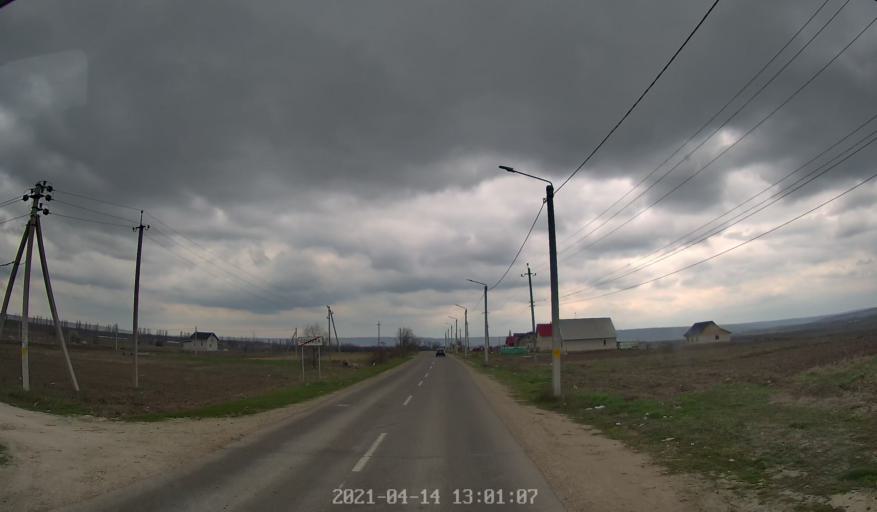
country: MD
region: Chisinau
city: Vadul lui Voda
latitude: 47.1342
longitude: 29.1181
